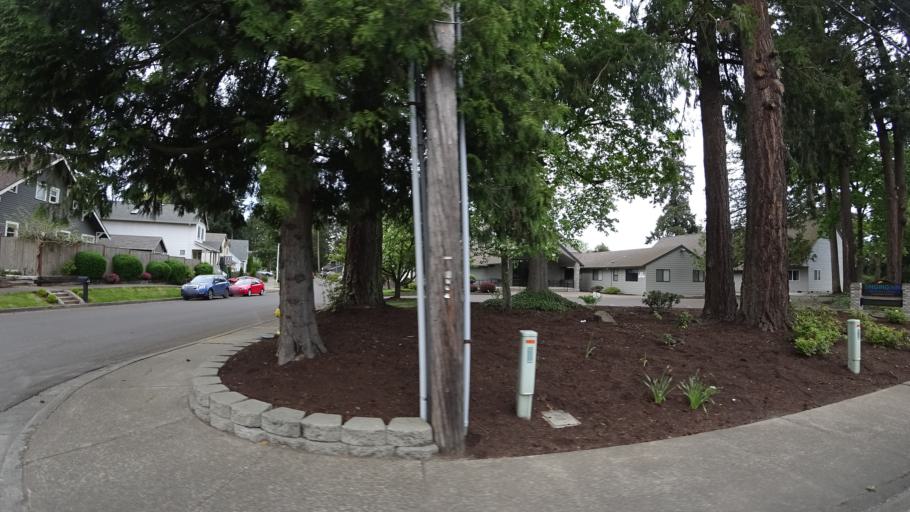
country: US
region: Oregon
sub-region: Washington County
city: Hillsboro
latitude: 45.4986
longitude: -122.9525
